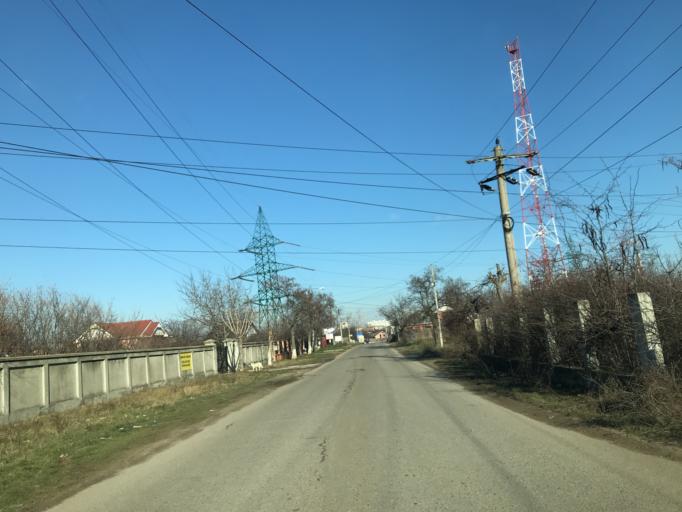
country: RO
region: Olt
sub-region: Municipiul Slatina
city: Slatina
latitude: 44.4156
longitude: 24.3625
